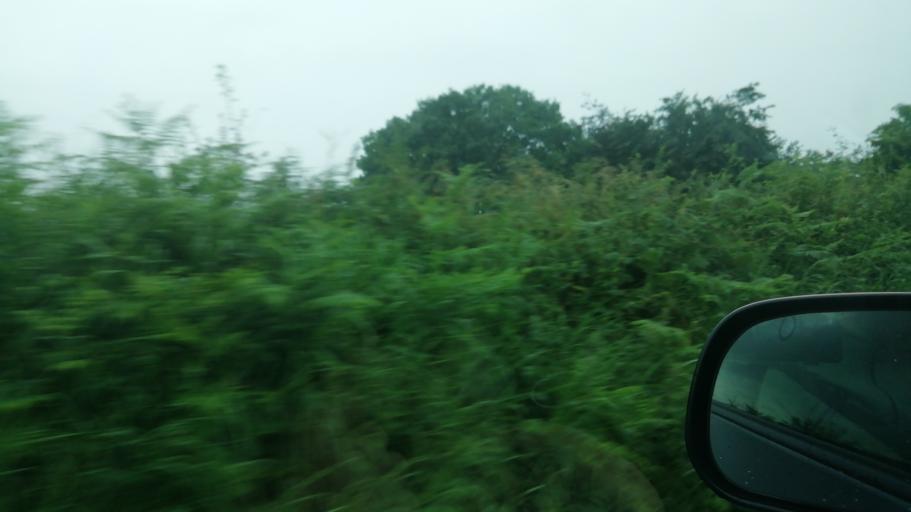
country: IE
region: Leinster
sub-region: Kilkenny
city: Thomastown
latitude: 52.6060
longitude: -7.1332
